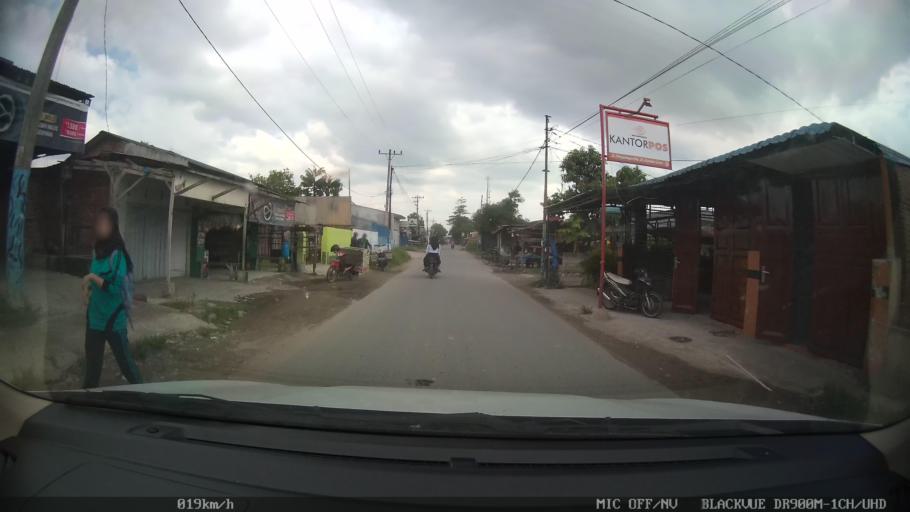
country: ID
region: North Sumatra
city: Sunggal
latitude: 3.6213
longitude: 98.6058
